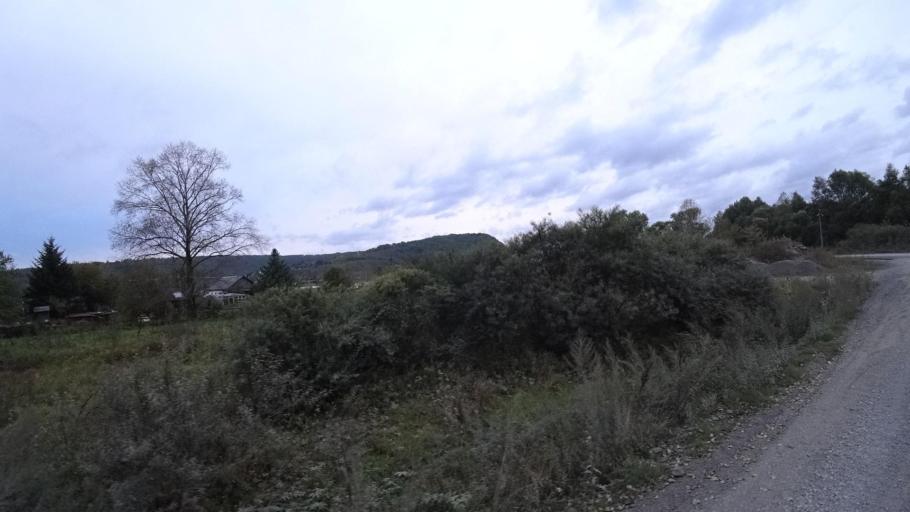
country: RU
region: Jewish Autonomous Oblast
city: Izvestkovyy
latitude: 48.9897
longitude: 131.5522
